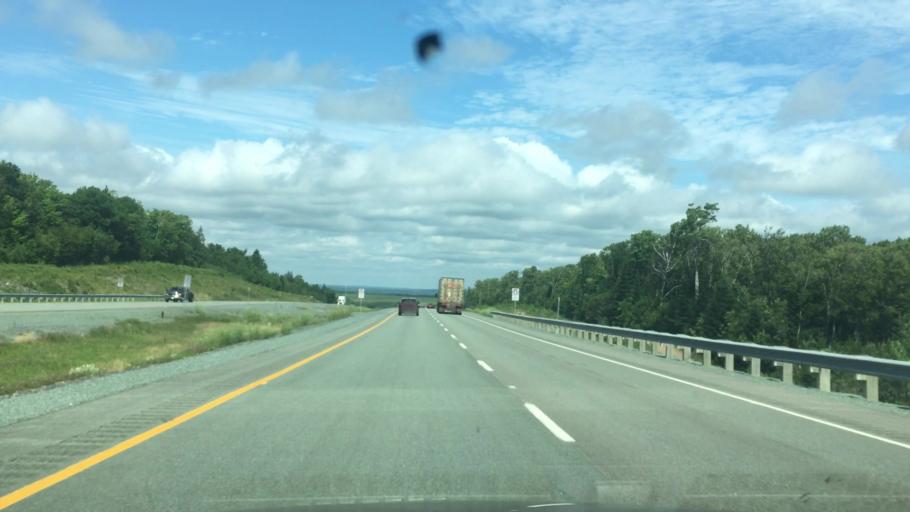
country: CA
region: Nova Scotia
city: Oxford
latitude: 45.5913
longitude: -63.7241
